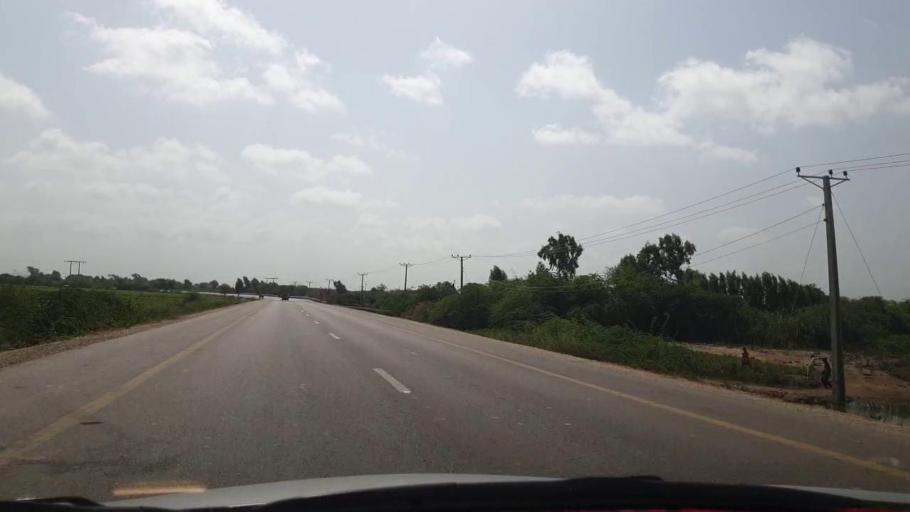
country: PK
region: Sindh
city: Talhar
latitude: 24.9120
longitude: 68.7314
